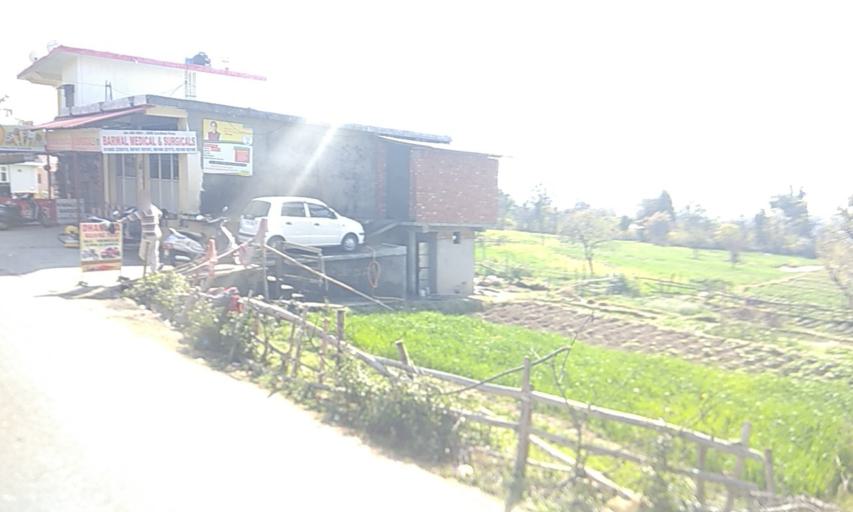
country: IN
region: Himachal Pradesh
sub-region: Kangra
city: Dharmsala
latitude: 32.1688
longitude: 76.3909
